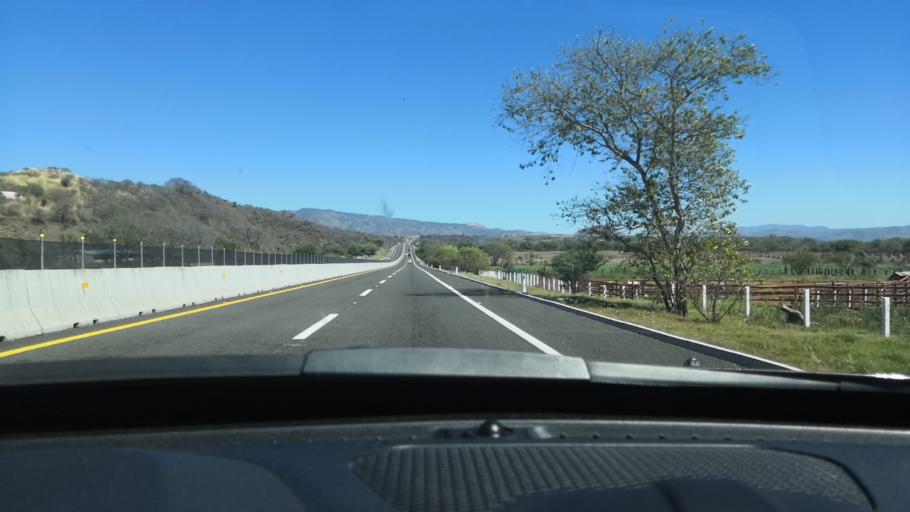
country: MX
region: Nayarit
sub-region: Ahuacatlan
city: Ahuacatlan
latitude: 21.0656
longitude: -104.4911
